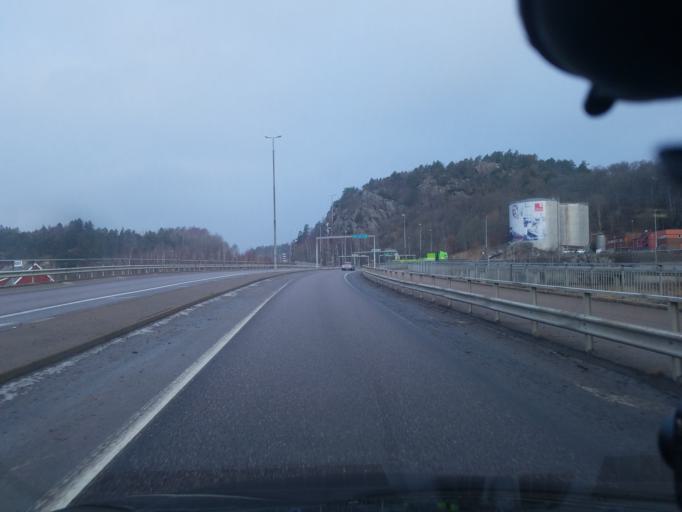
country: SE
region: Vaestra Goetaland
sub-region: Uddevalla Kommun
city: Uddevalla
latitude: 58.3547
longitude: 11.9130
